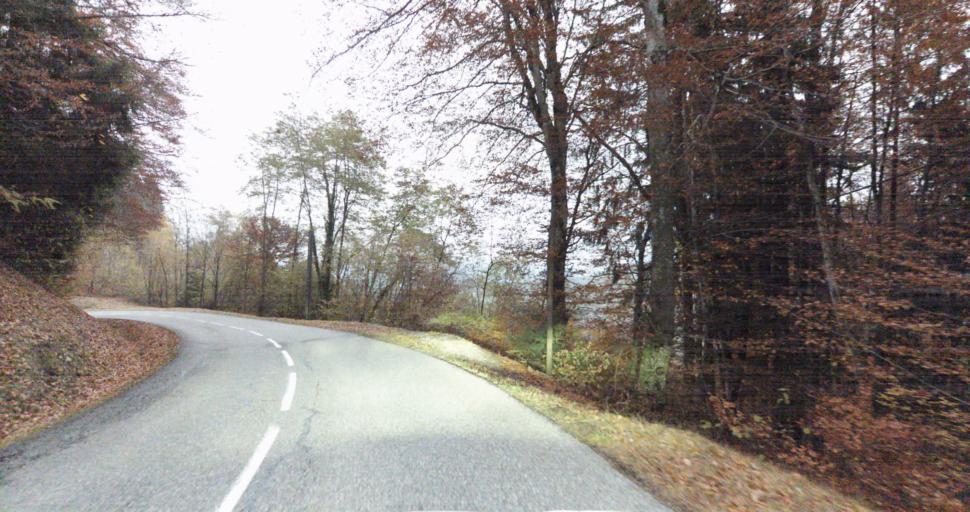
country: FR
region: Rhone-Alpes
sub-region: Departement de la Haute-Savoie
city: Saint-Jorioz
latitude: 45.7982
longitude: 6.1376
